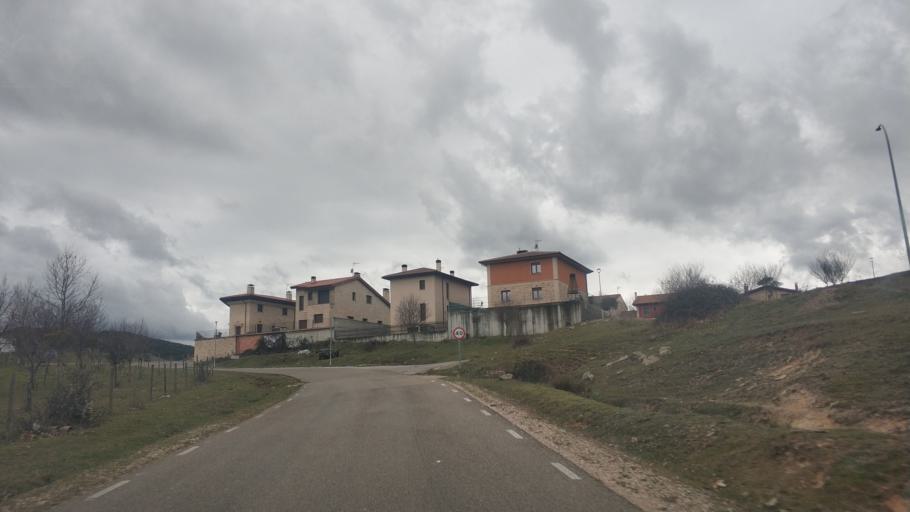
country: ES
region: Castille and Leon
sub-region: Provincia de Burgos
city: Canicosa de la Sierra
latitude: 41.9398
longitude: -3.0384
